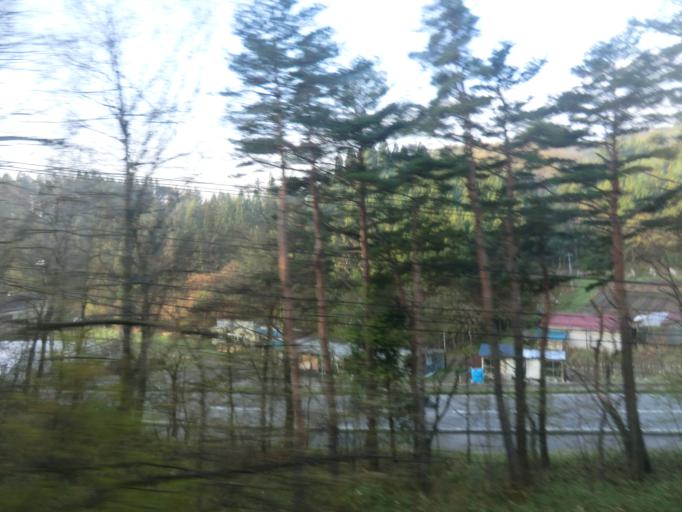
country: JP
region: Aomori
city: Hachinohe
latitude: 40.1340
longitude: 141.7778
